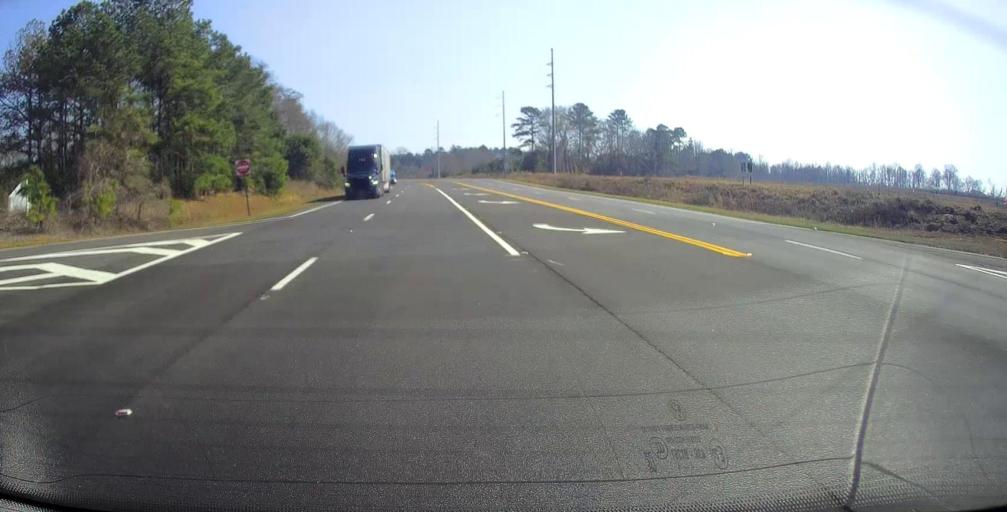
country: US
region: Georgia
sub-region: Houston County
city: Perry
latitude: 32.4900
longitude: -83.7370
